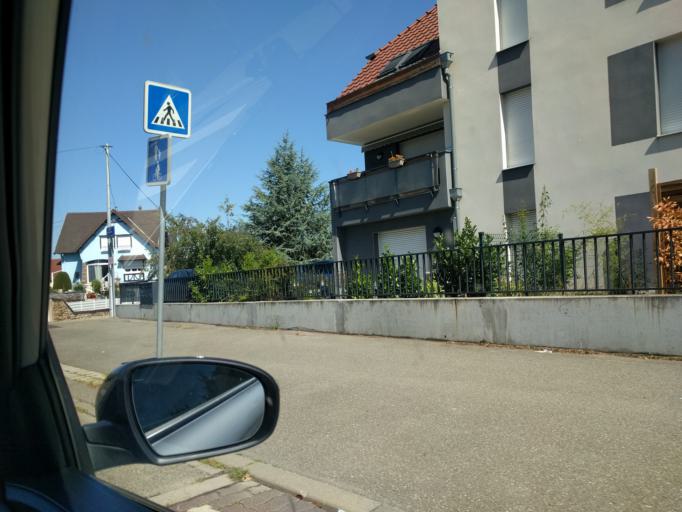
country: FR
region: Alsace
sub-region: Departement du Bas-Rhin
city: Geispolsheim
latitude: 48.5185
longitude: 7.6480
